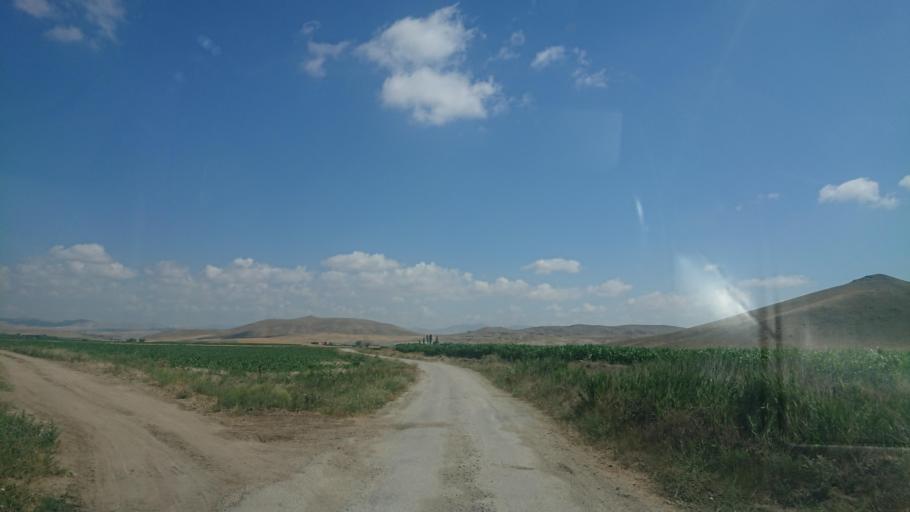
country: TR
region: Aksaray
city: Sariyahsi
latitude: 38.9830
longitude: 33.9073
